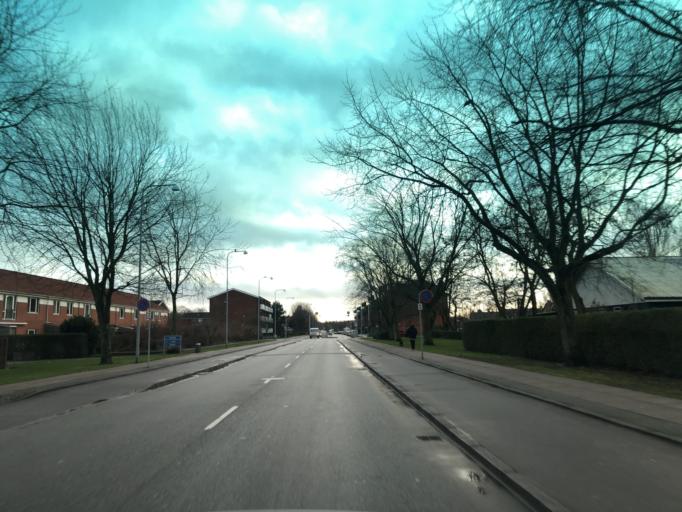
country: DK
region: Capital Region
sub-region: Tarnby Kommune
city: Tarnby
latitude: 55.6376
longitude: 12.6089
